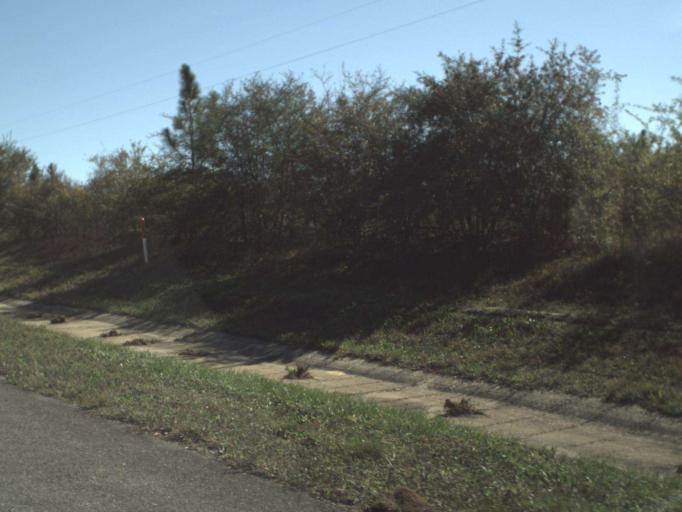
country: US
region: Florida
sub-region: Okaloosa County
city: Crestview
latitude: 30.8503
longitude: -86.7798
